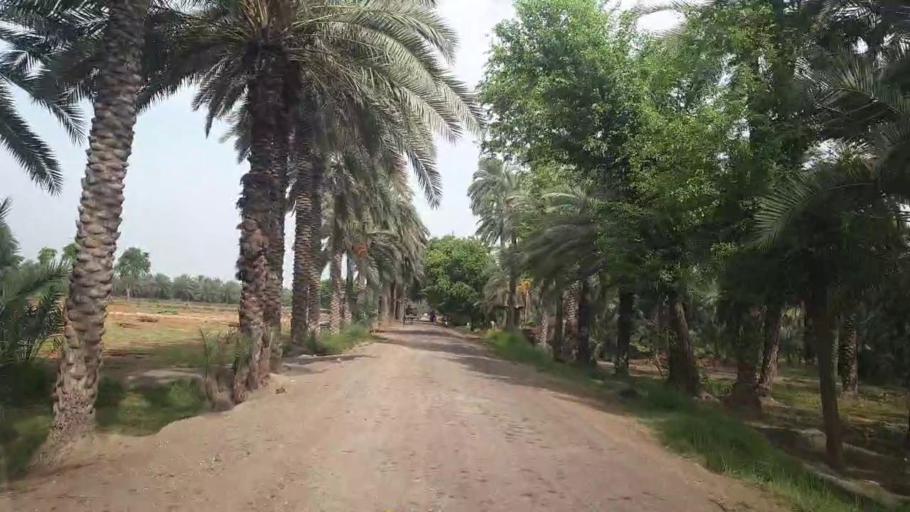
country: PK
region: Sindh
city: Sukkur
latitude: 27.6416
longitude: 68.8225
